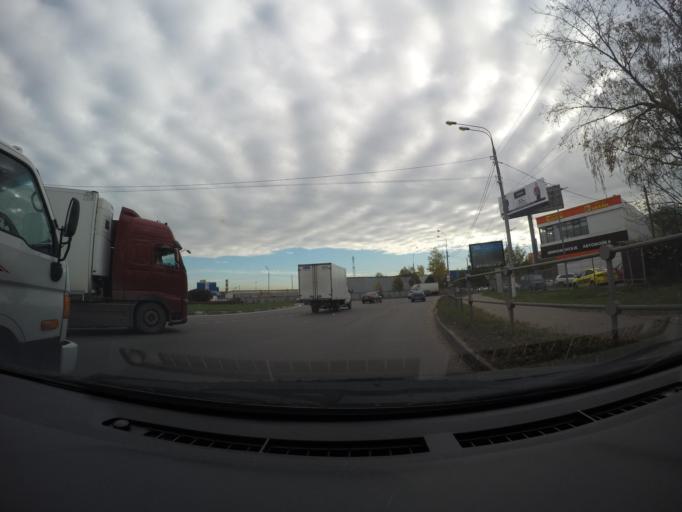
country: RU
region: Moskovskaya
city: Mytishchi
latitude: 55.9323
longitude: 37.7519
